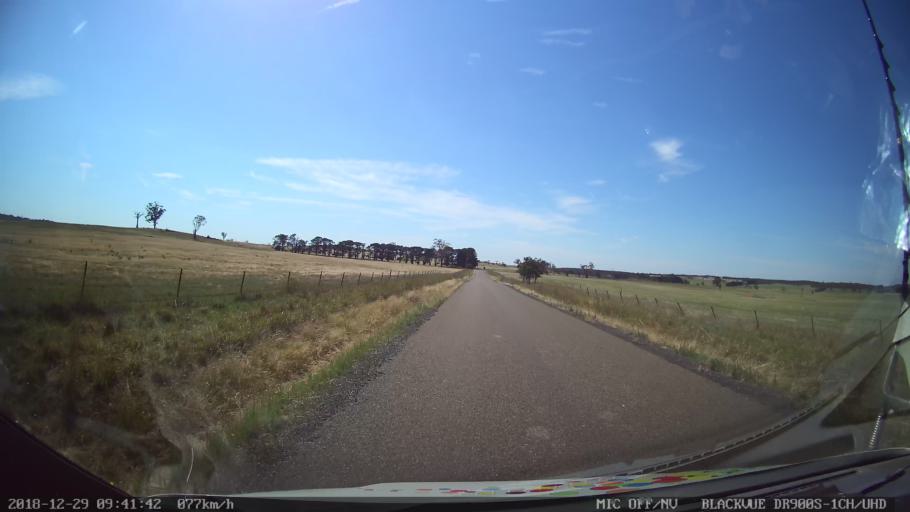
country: AU
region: New South Wales
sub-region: Upper Lachlan Shire
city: Crookwell
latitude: -34.6629
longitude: 149.4142
